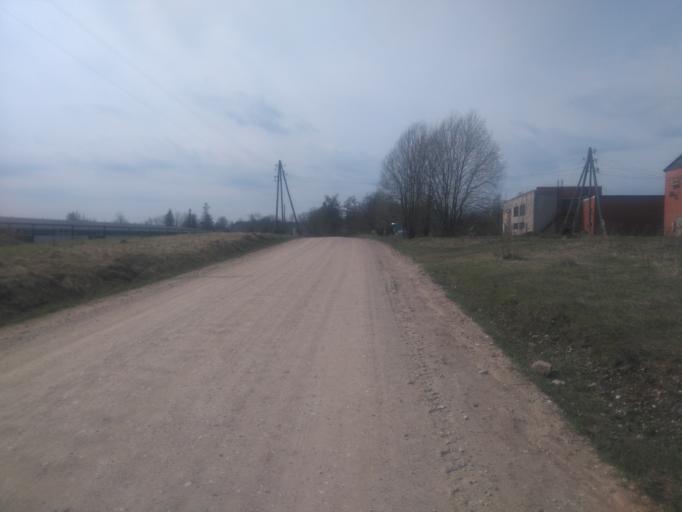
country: LV
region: Vecpiebalga
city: Vecpiebalga
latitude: 57.0211
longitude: 25.8363
